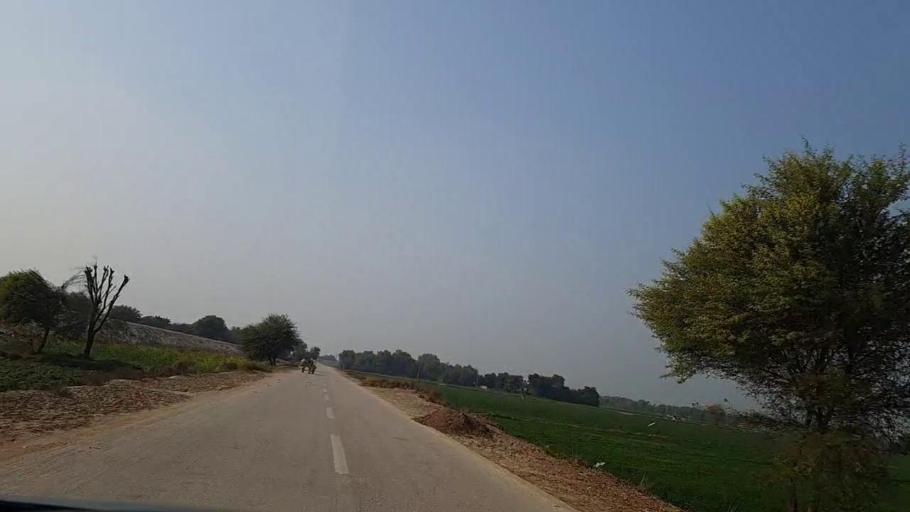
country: PK
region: Sindh
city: Sann
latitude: 26.1509
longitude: 68.1255
